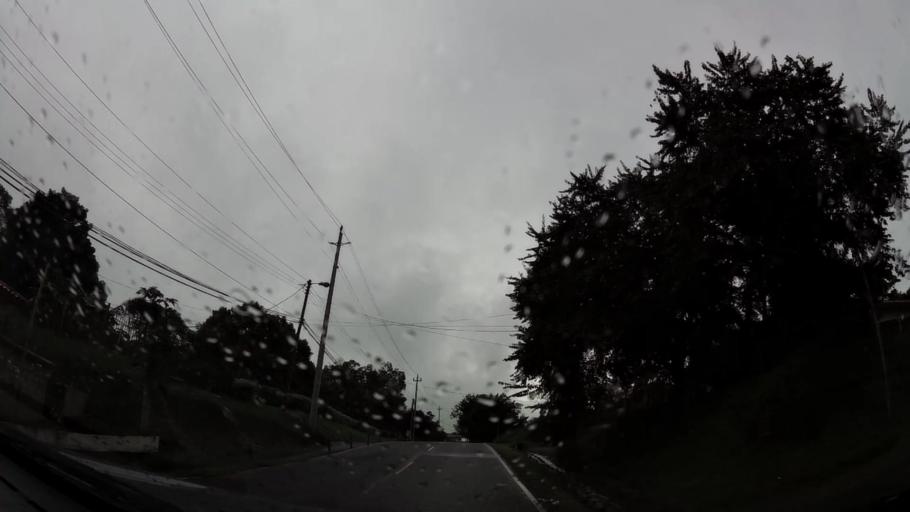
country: PA
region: Veraguas
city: Santiago de Veraguas
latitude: 8.0920
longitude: -80.9569
